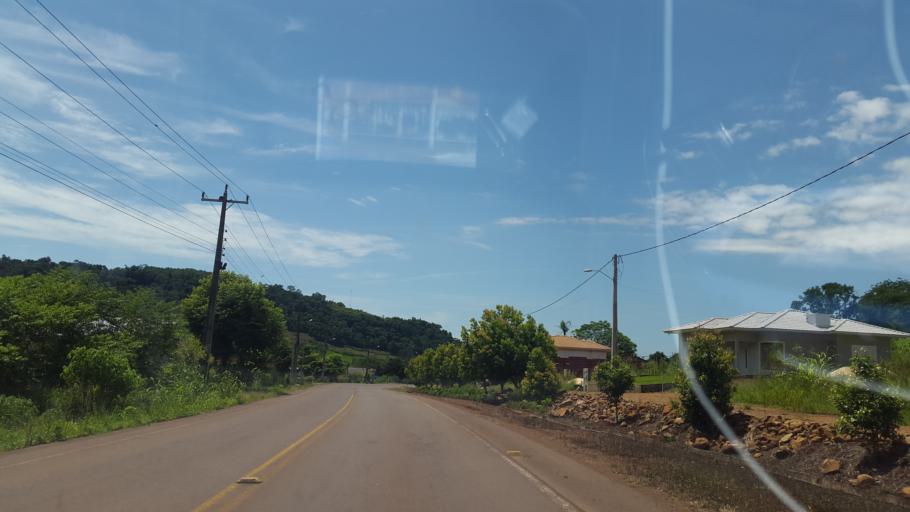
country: BR
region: Rio Grande do Sul
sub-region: Frederico Westphalen
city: Frederico Westphalen
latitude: -27.0655
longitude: -53.4322
